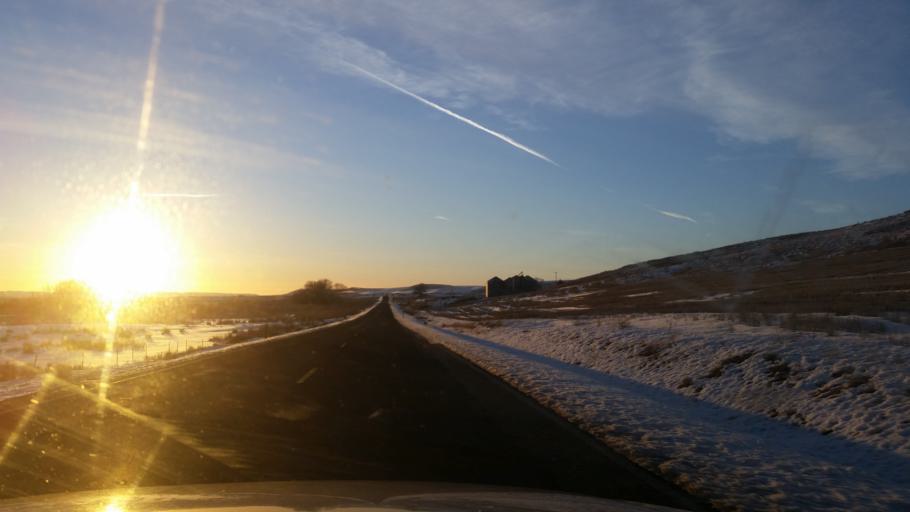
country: US
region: Washington
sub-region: Spokane County
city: Cheney
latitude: 47.1195
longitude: -117.7782
